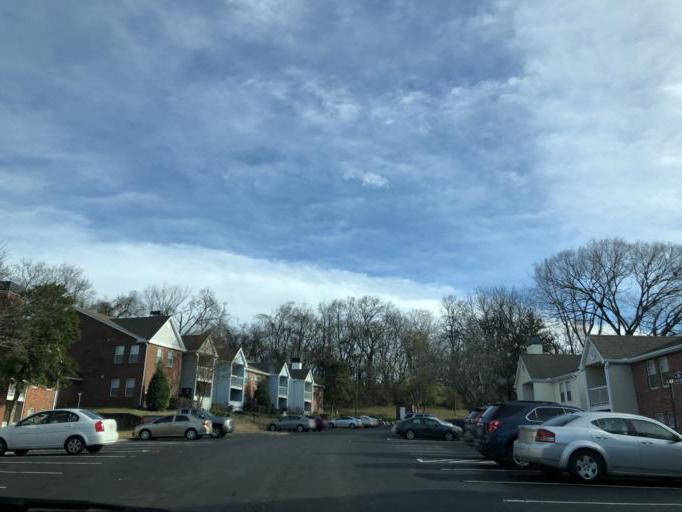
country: US
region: Tennessee
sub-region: Davidson County
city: Lakewood
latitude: 36.1479
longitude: -86.6223
